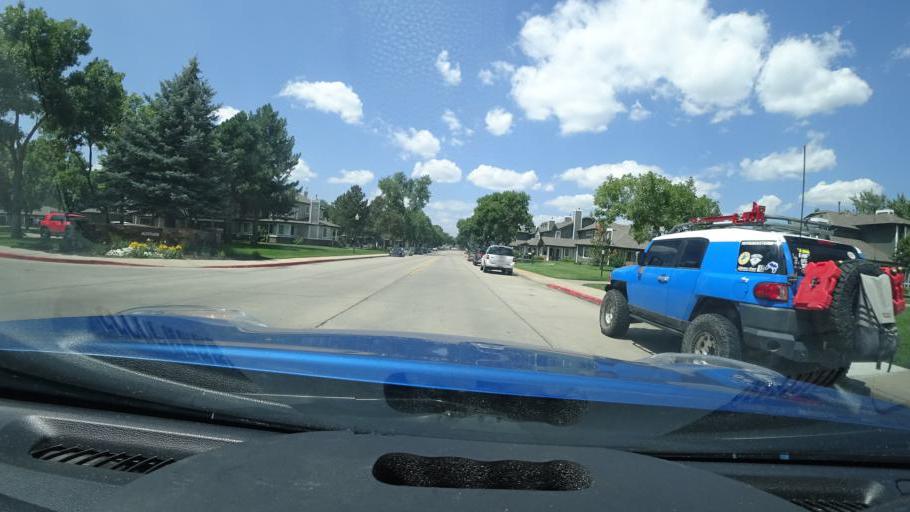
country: US
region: Colorado
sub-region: Arapahoe County
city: Glendale
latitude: 39.6979
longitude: -104.8838
